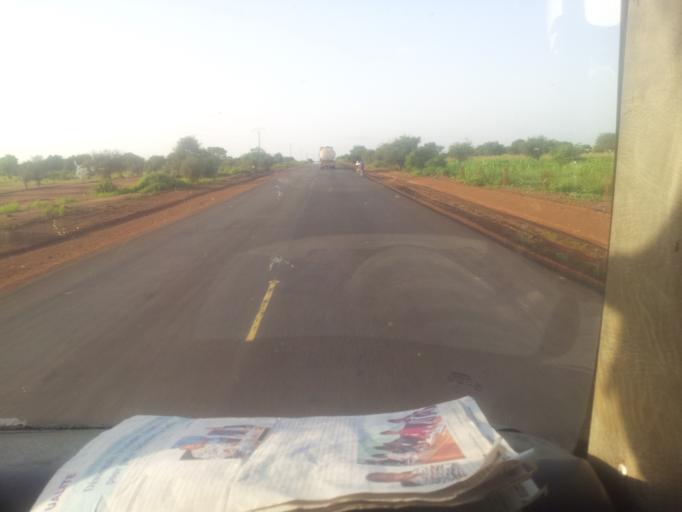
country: BF
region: Centre-Est
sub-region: Kouritenga Province
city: Koupela
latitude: 11.9855
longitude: -0.3679
